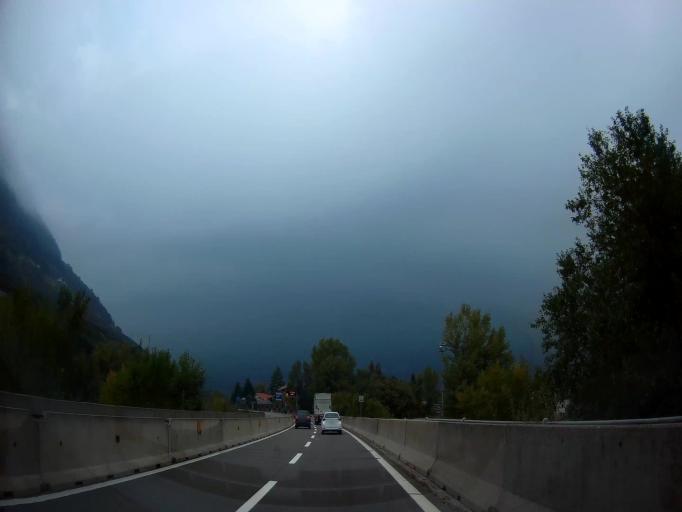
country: IT
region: Trentino-Alto Adige
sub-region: Bolzano
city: Marlengo
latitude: 46.6640
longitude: 11.1442
